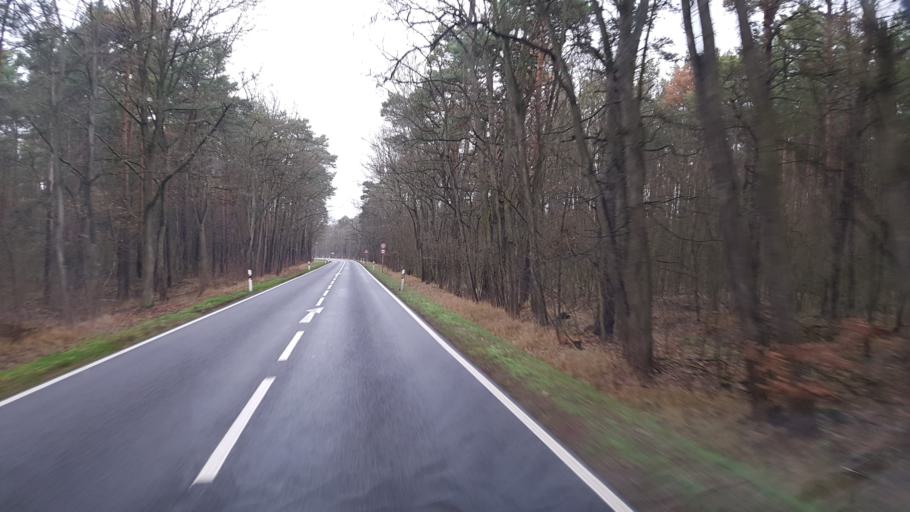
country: DE
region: Brandenburg
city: Calau
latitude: 51.7193
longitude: 14.0123
